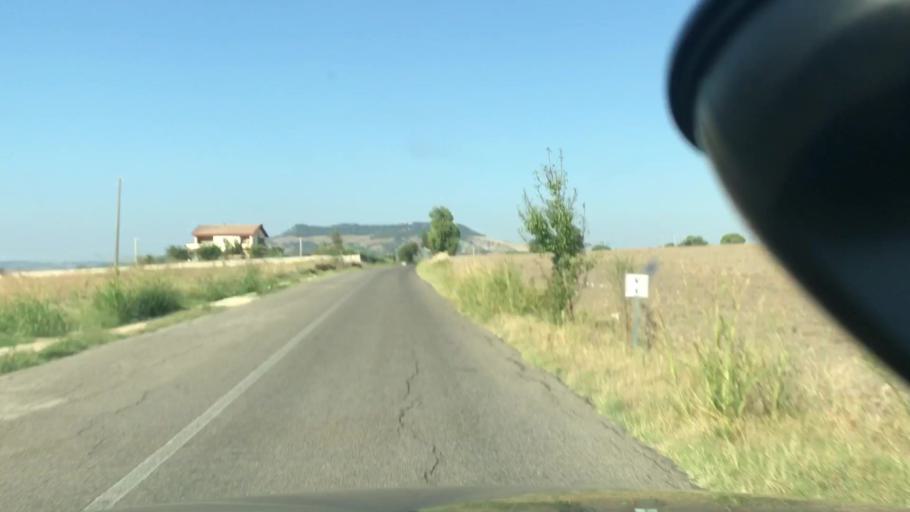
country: IT
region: Basilicate
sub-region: Provincia di Matera
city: La Martella
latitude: 40.6587
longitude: 16.5377
